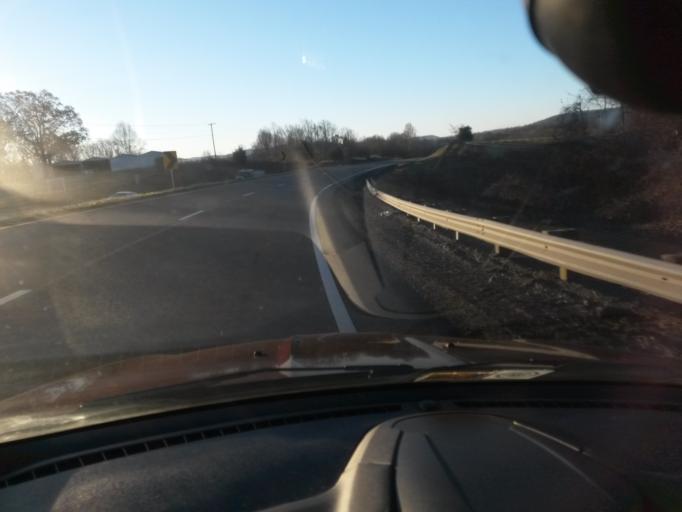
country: US
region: Virginia
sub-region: Franklin County
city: Henry Fork
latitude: 36.9395
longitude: -79.8740
